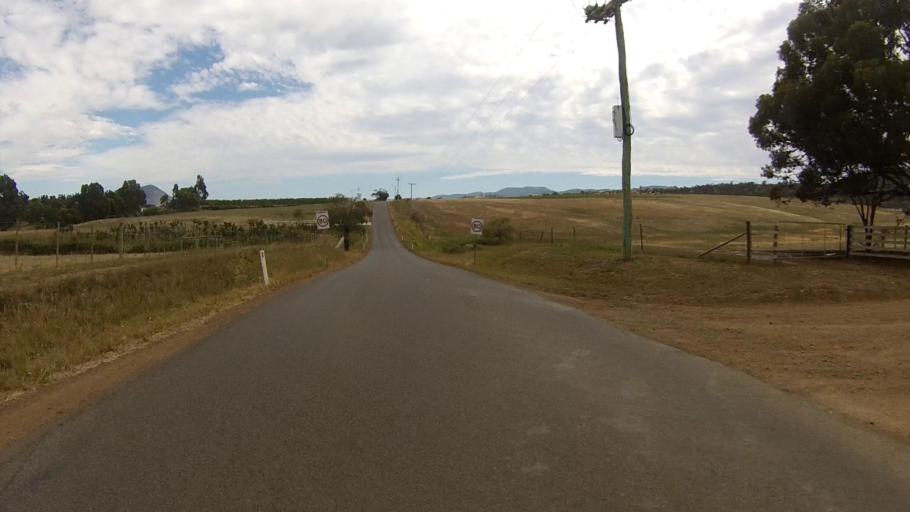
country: AU
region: Tasmania
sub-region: Clarence
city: Cambridge
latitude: -42.7292
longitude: 147.4489
